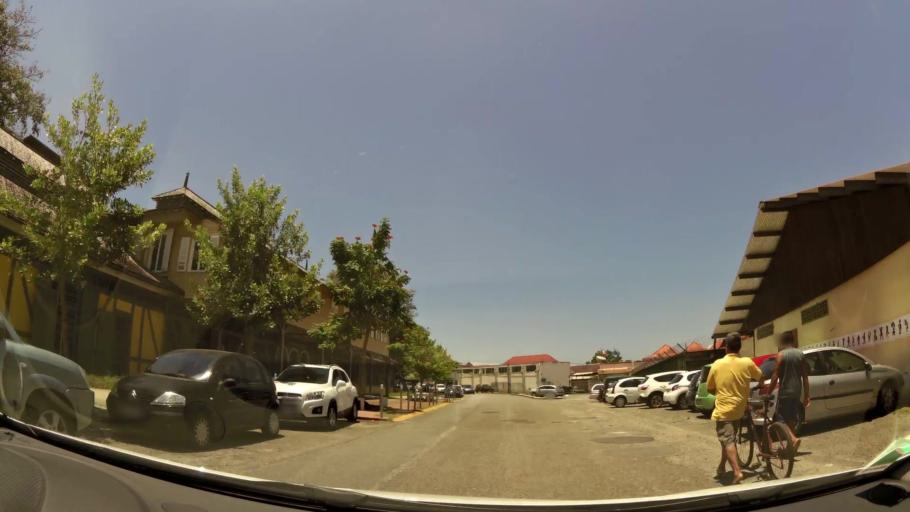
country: GF
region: Guyane
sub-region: Guyane
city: Cayenne
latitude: 4.9366
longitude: -52.3371
